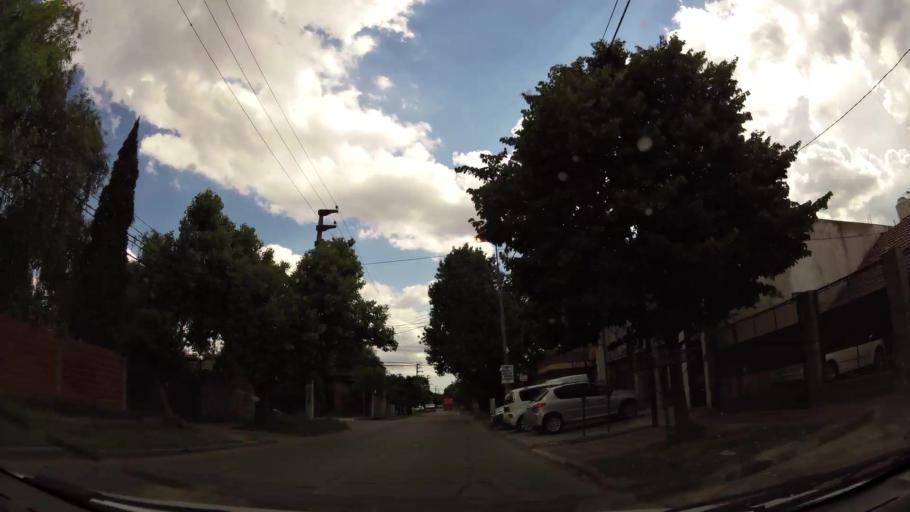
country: AR
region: Buenos Aires
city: Ituzaingo
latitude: -34.6365
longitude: -58.6694
